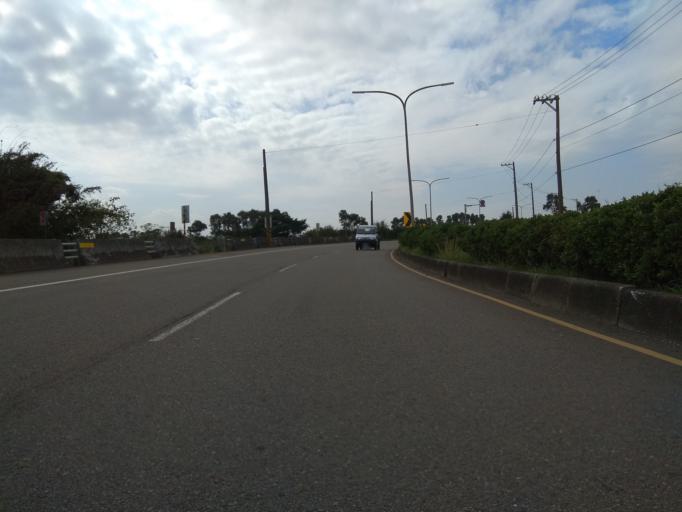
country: TW
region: Taiwan
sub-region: Hsinchu
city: Zhubei
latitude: 24.9730
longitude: 121.0265
